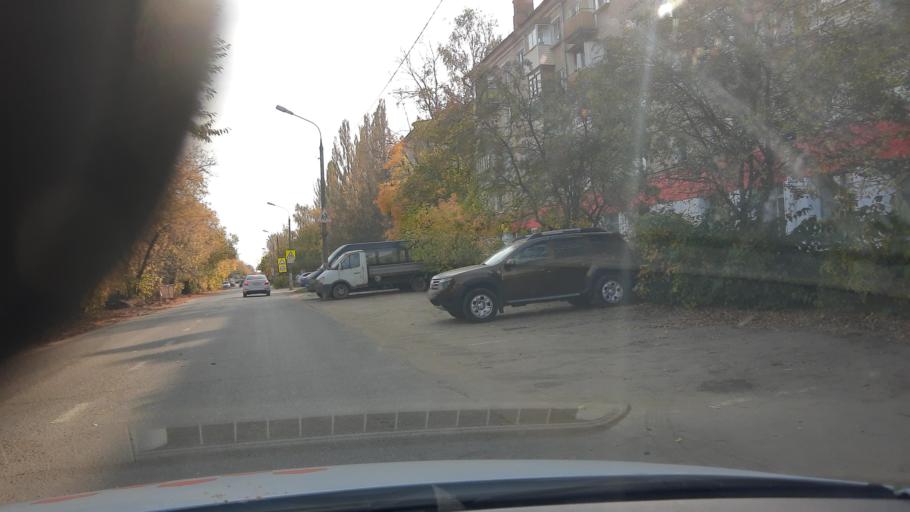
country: RU
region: Moskovskaya
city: Elektrostal'
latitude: 55.8018
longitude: 38.4418
